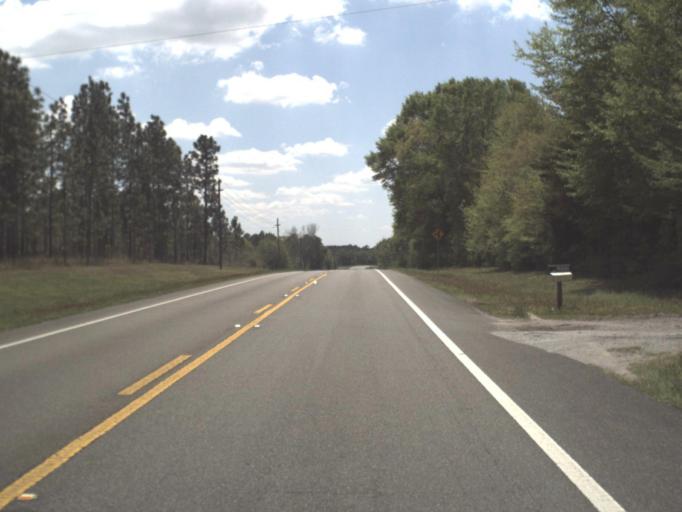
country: US
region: Florida
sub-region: Okaloosa County
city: Crestview
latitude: 30.8746
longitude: -86.6659
